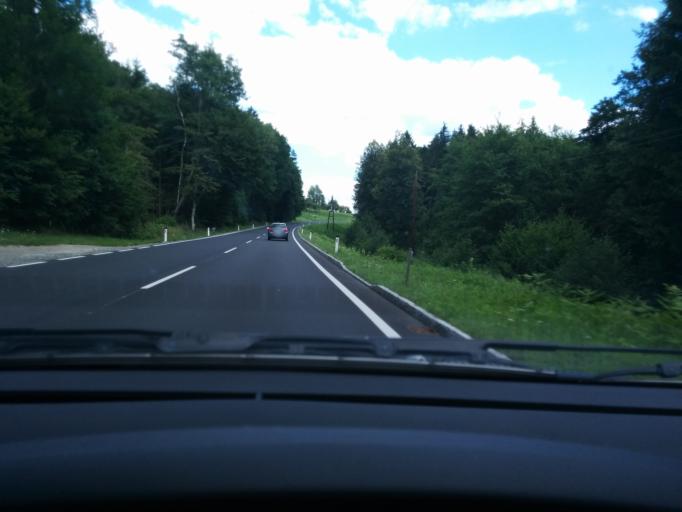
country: AT
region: Styria
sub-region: Politischer Bezirk Weiz
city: Oberrettenbach
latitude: 47.1620
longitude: 15.7756
